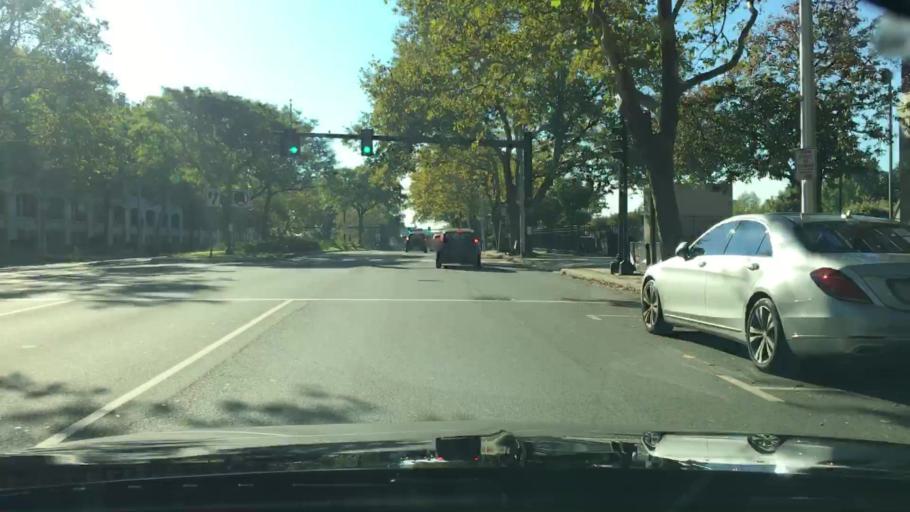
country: US
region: Connecticut
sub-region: Fairfield County
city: Bridgeport
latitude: 41.1749
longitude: -73.1921
